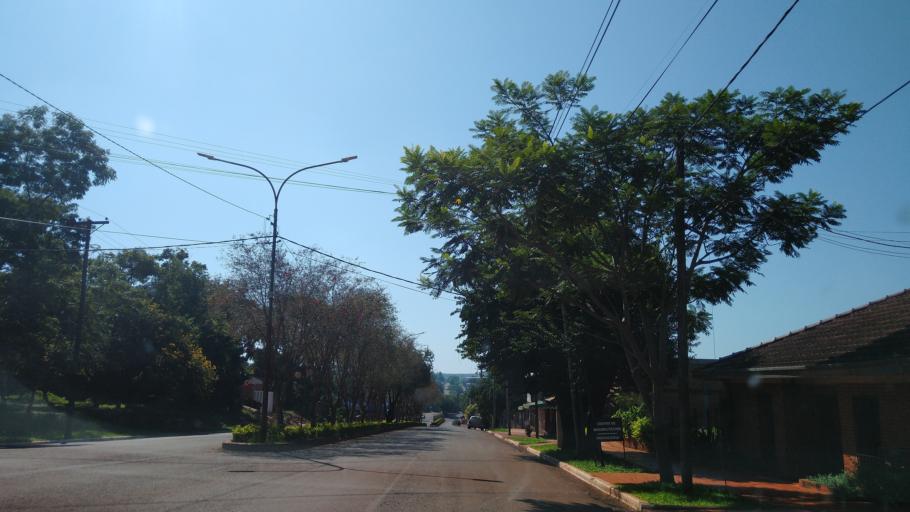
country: AR
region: Misiones
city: Puerto Esperanza
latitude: -26.0229
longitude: -54.6153
